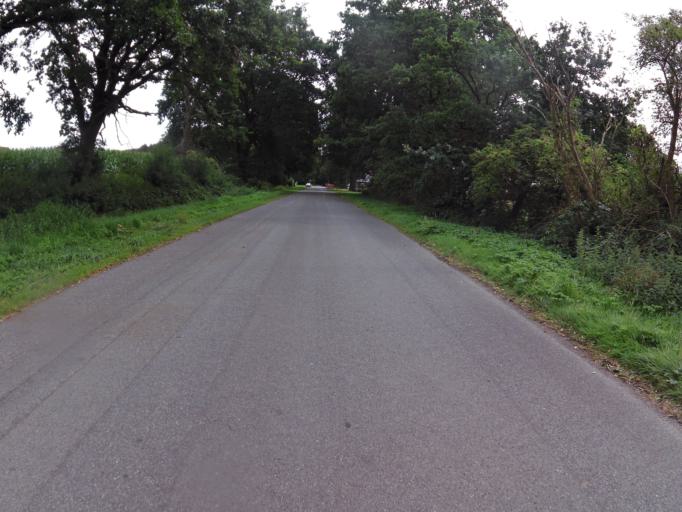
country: DE
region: Lower Saxony
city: Lunestedt
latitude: 53.4912
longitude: 8.7280
